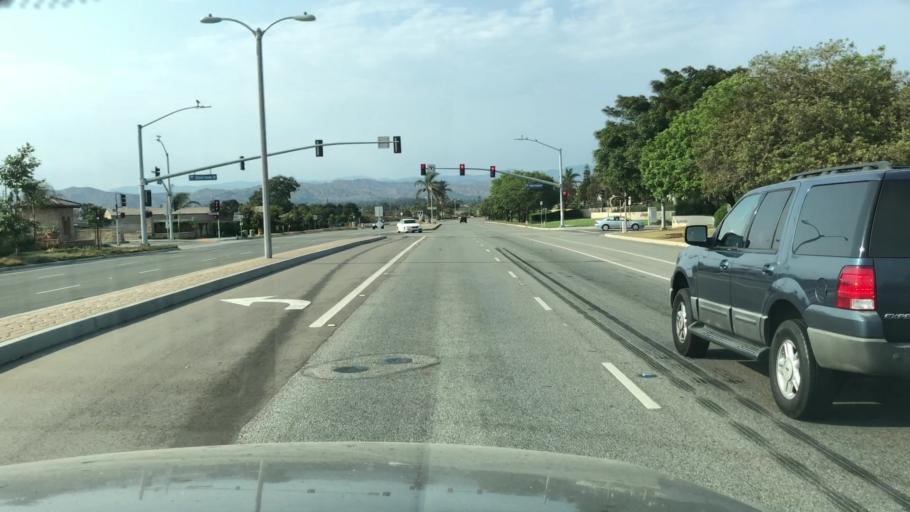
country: US
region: California
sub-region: Ventura County
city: El Rio
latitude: 34.2316
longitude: -119.1944
